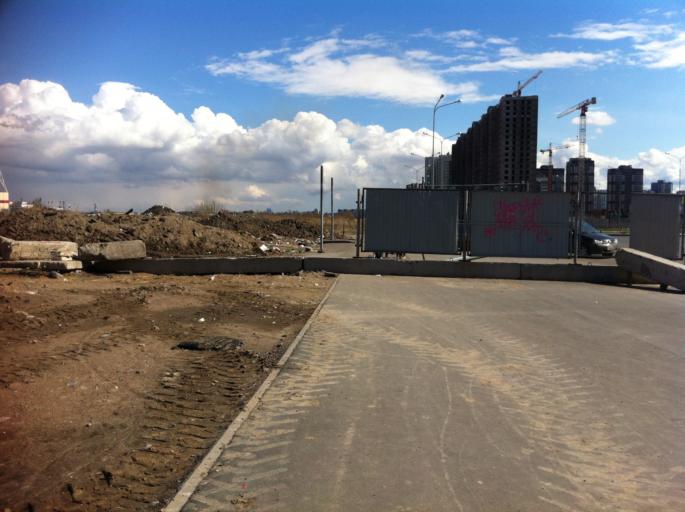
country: RU
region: St.-Petersburg
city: Uritsk
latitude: 59.8688
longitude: 30.1676
